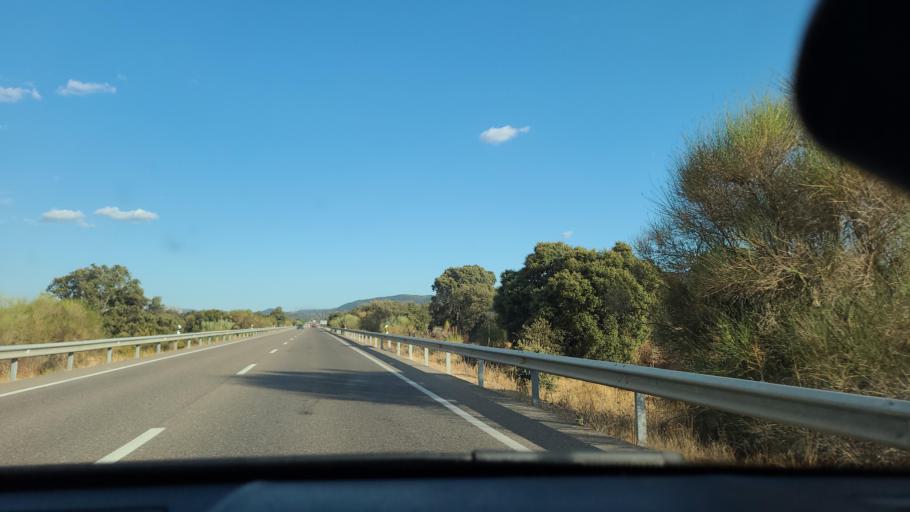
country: ES
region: Andalusia
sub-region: Province of Cordoba
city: Belmez
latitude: 38.2214
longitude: -5.1532
